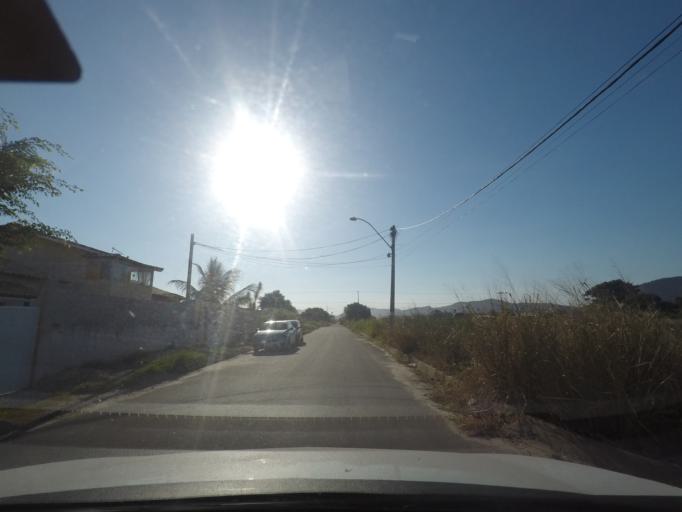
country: BR
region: Rio de Janeiro
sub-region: Marica
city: Marica
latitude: -22.9619
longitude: -42.9379
